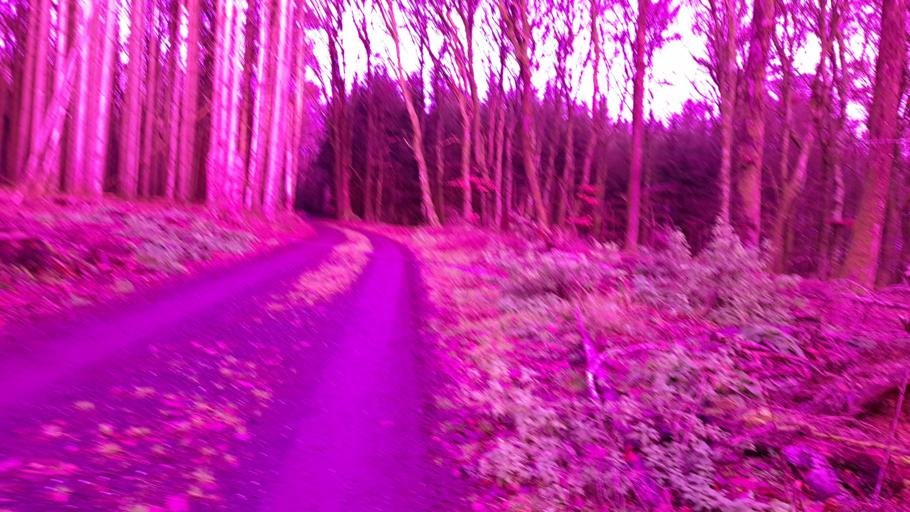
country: DE
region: Rheinland-Pfalz
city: Dasburg
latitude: 50.0736
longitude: 6.1098
